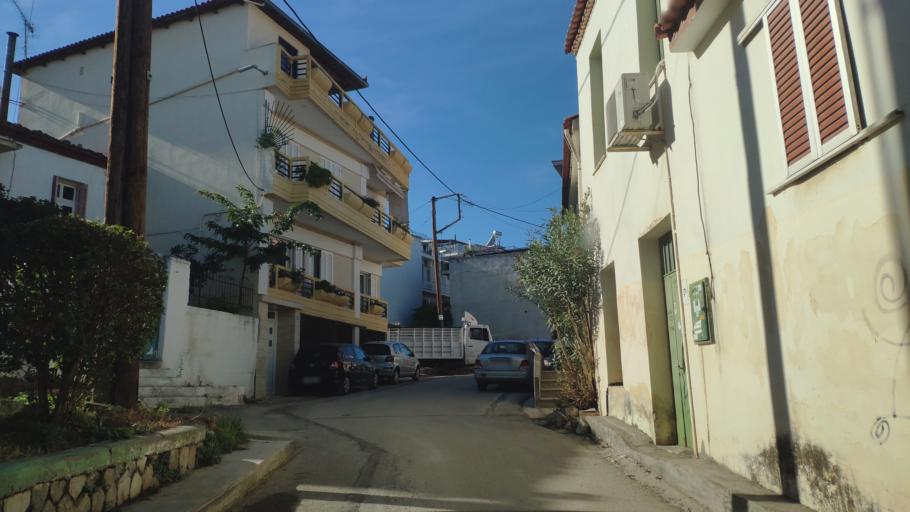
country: GR
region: Central Greece
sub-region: Nomos Voiotias
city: Livadeia
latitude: 38.4365
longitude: 22.8780
